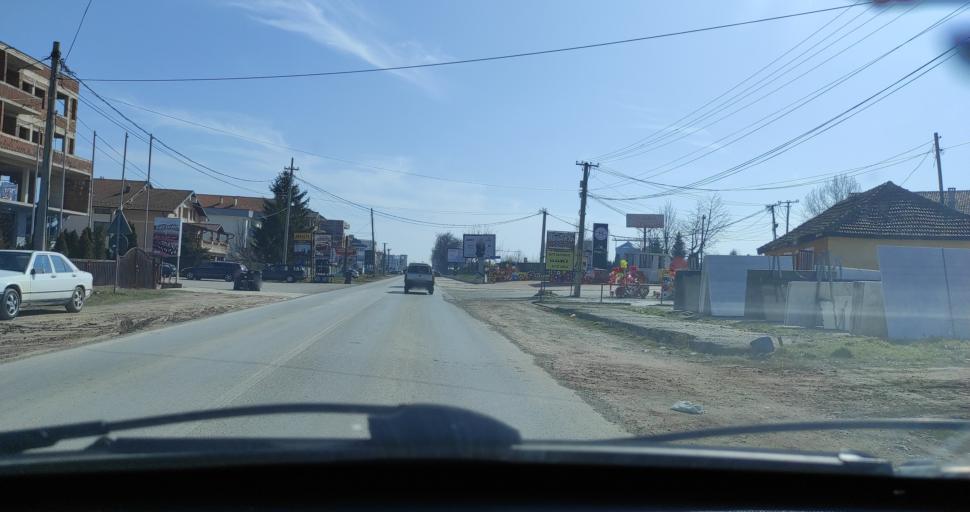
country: XK
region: Pec
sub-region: Komuna e Pejes
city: Peje
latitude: 42.6405
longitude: 20.2947
